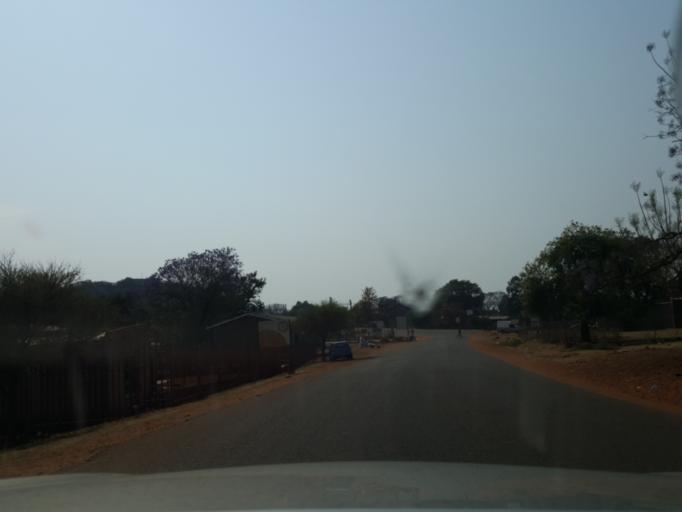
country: BW
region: South East
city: Lobatse
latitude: -25.2843
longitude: 25.8862
